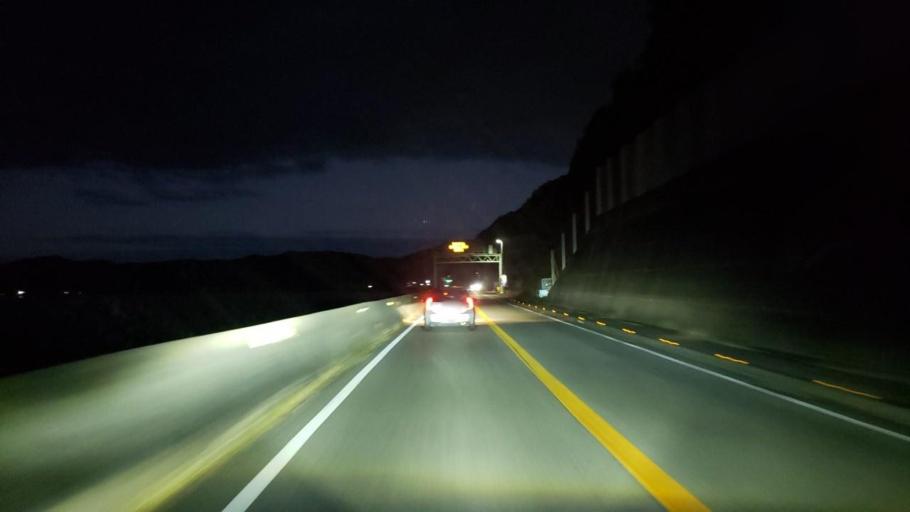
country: JP
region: Tokushima
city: Narutocho-mitsuishi
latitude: 34.2234
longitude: 134.5504
